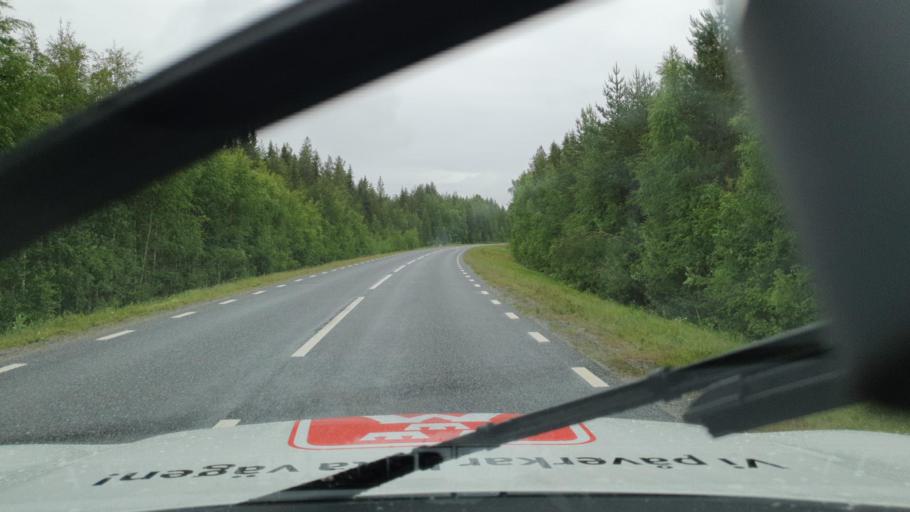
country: SE
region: Vaesterbotten
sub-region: Asele Kommun
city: Asele
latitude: 63.9843
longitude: 17.2652
